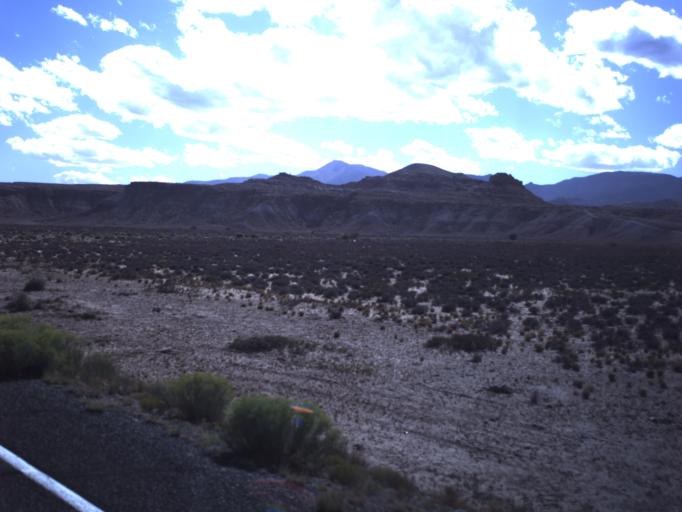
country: US
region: Utah
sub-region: Wayne County
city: Loa
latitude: 38.1114
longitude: -110.6246
